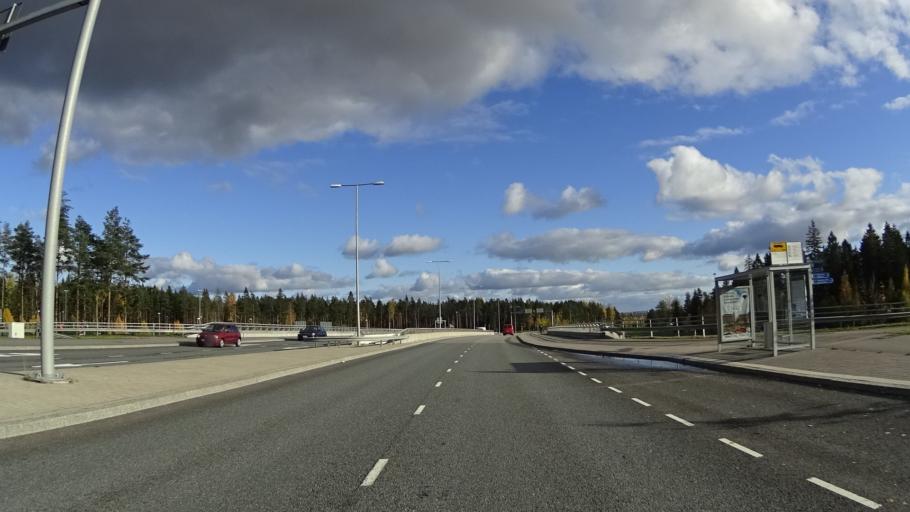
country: FI
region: Uusimaa
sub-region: Helsinki
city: Vantaa
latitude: 60.3018
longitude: 24.9590
